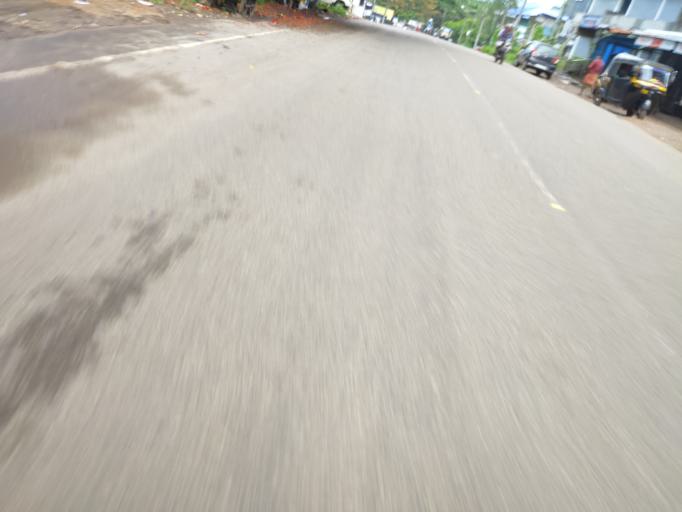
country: IN
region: Kerala
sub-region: Malappuram
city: Manjeri
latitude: 11.1945
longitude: 76.2395
